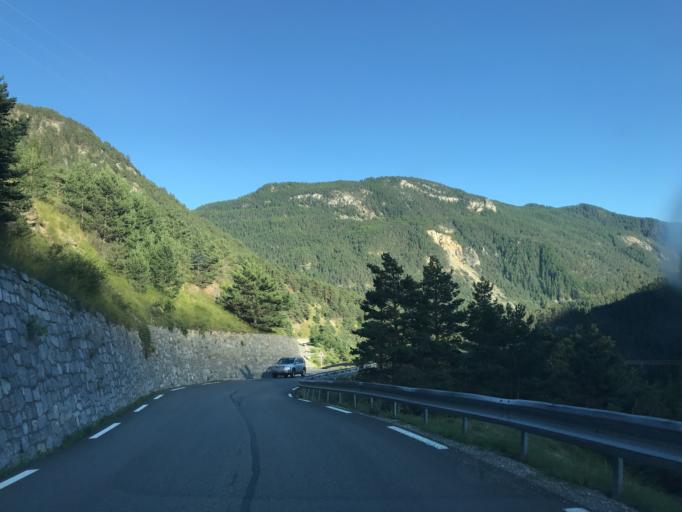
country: FR
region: Provence-Alpes-Cote d'Azur
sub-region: Departement des Hautes-Alpes
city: Guillestre
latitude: 44.7518
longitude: 6.7622
